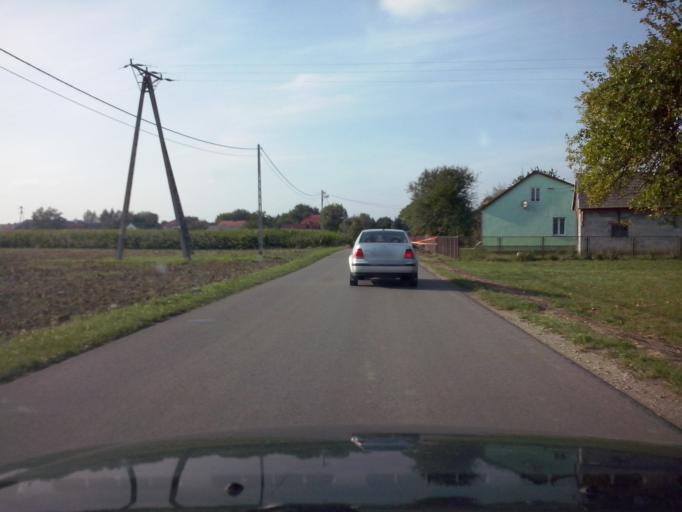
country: PL
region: Subcarpathian Voivodeship
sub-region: Powiat nizanski
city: Krzeszow
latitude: 50.3981
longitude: 22.3190
